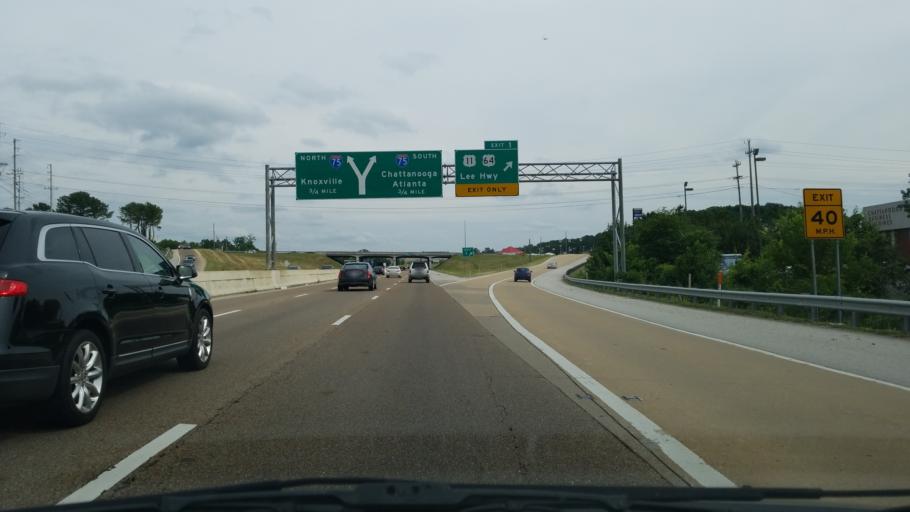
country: US
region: Tennessee
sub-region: Hamilton County
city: East Brainerd
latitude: 35.0351
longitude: -85.1837
